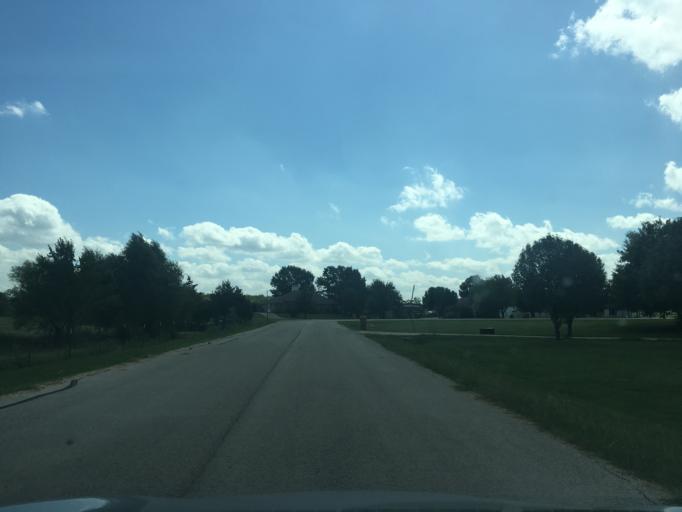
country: US
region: Texas
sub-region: Dallas County
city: Sachse
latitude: 32.9534
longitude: -96.5565
